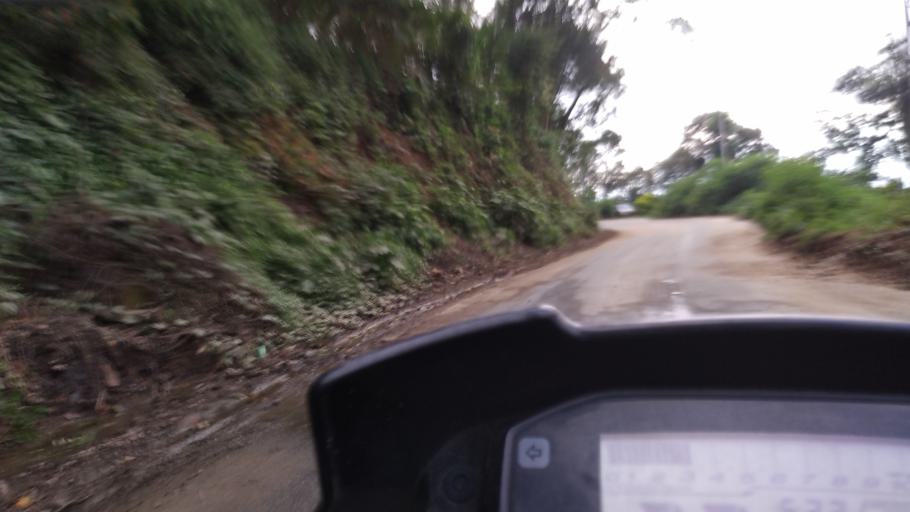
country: IN
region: Tamil Nadu
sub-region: Theni
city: Bodinayakkanur
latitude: 10.0133
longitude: 77.2385
